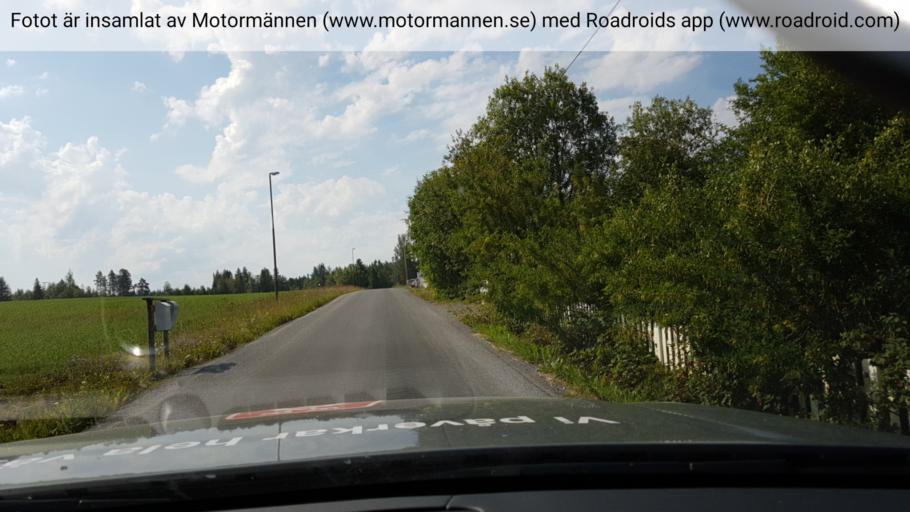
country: SE
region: Jaemtland
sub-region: OEstersunds Kommun
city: Ostersund
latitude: 63.1519
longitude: 14.5462
